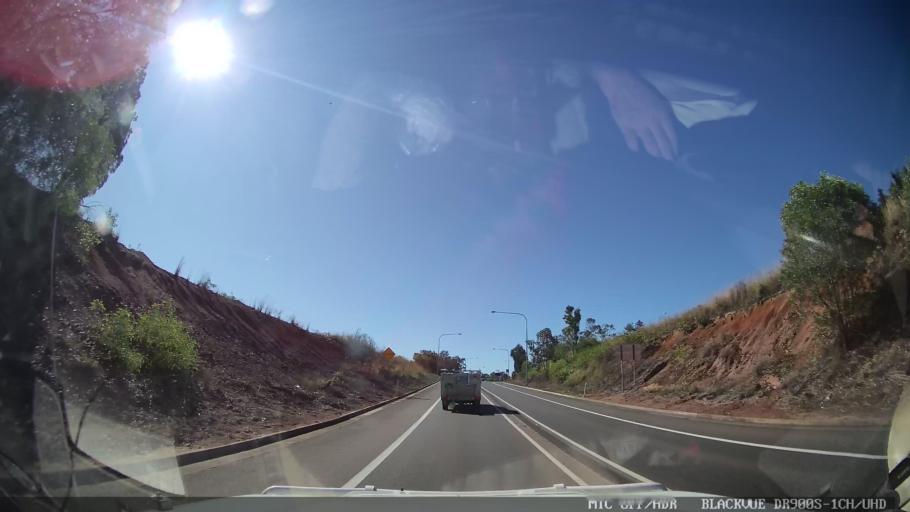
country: AU
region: Queensland
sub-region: Fraser Coast
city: Maryborough
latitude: -25.5165
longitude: 152.6698
